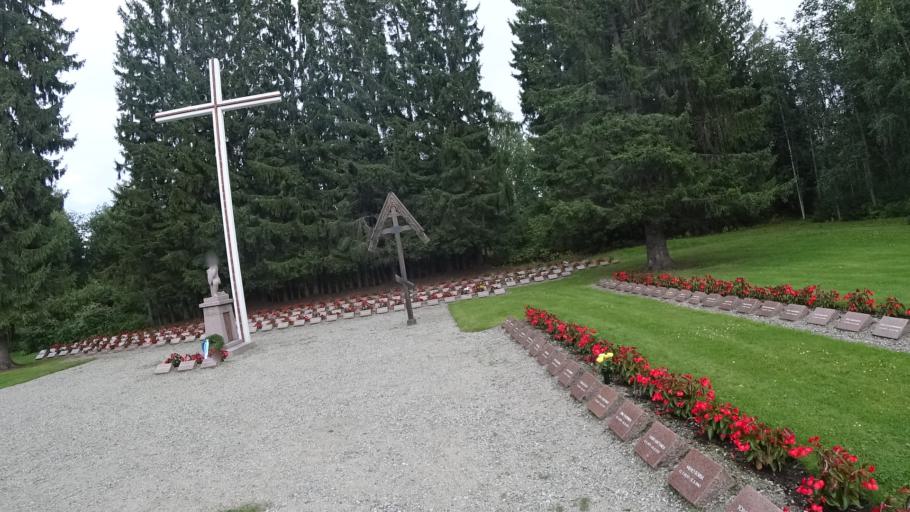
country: FI
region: North Karelia
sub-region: Joensuu
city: Ilomantsi
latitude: 62.6776
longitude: 30.9172
